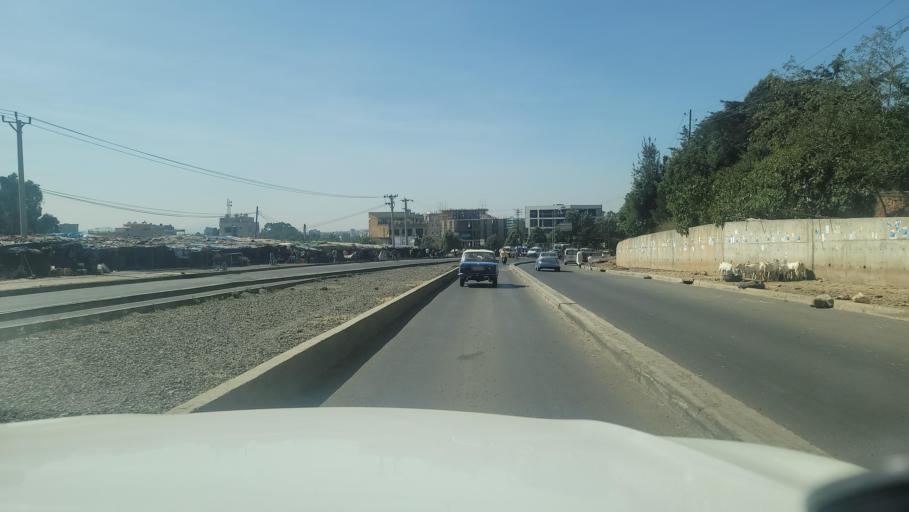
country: ET
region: Adis Abeba
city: Addis Ababa
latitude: 9.0256
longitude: 38.8198
